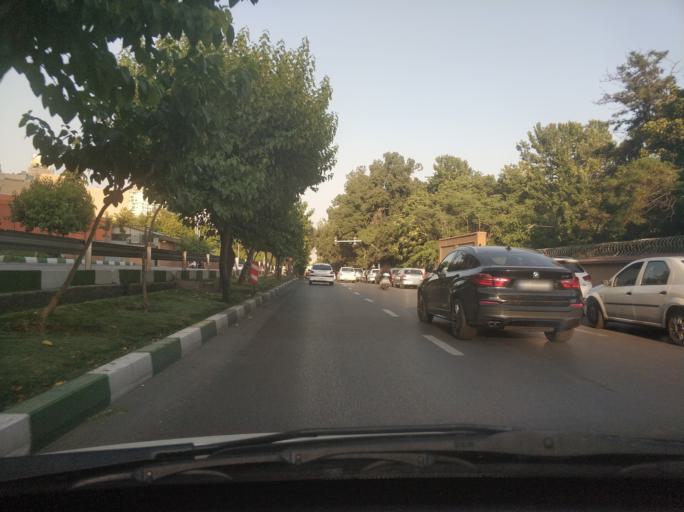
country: IR
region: Tehran
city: Tajrish
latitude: 35.8007
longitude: 51.4645
